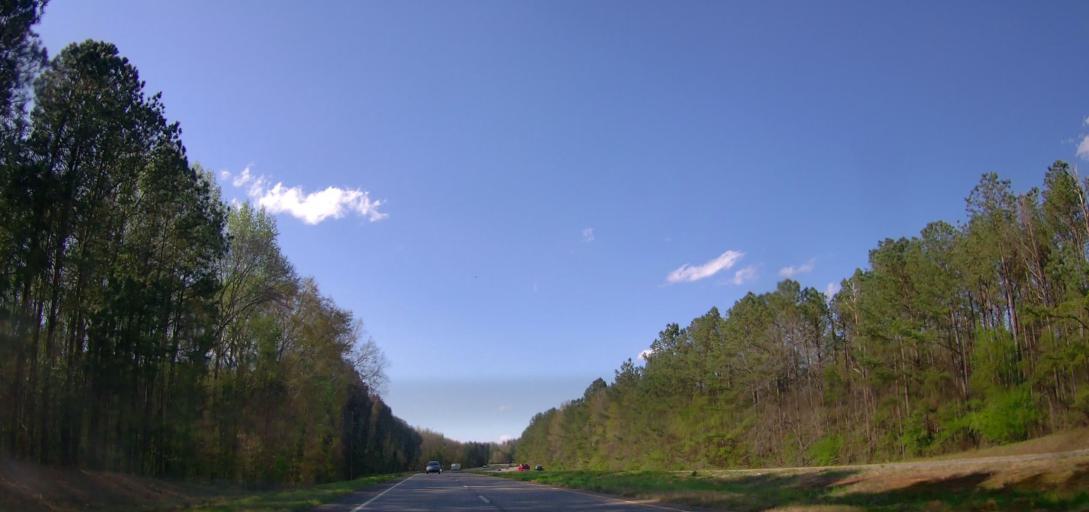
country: US
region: Georgia
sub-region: Baldwin County
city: Hardwick
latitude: 33.0393
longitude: -83.2538
